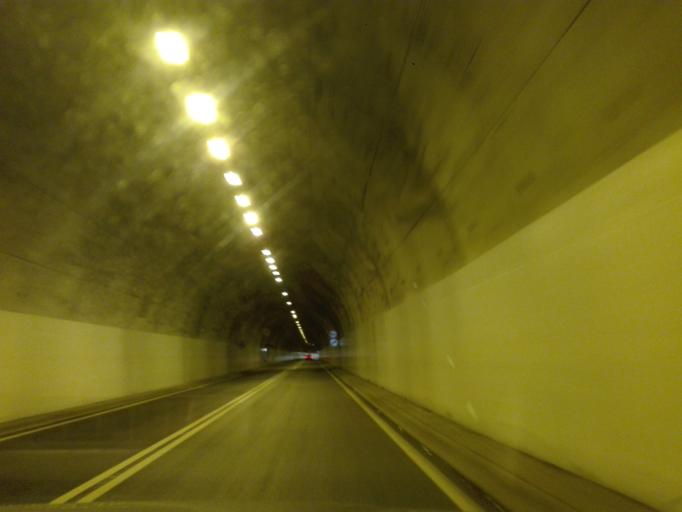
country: PT
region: Madeira
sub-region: Santana
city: Santana
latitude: 32.7670
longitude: -16.8391
